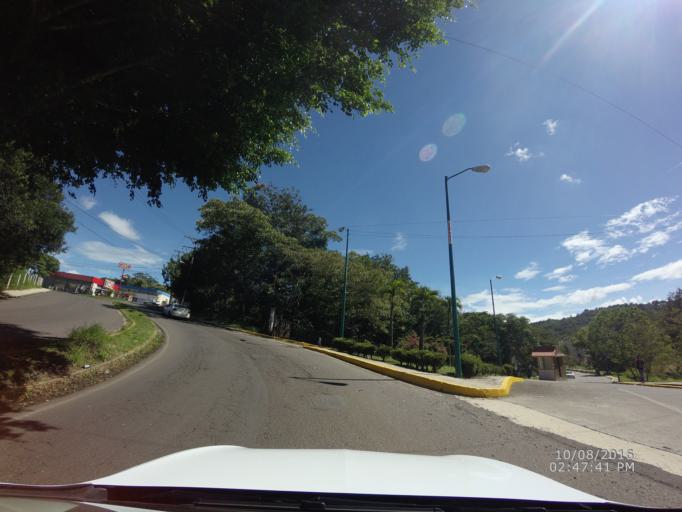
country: MX
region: Veracruz
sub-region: Xalapa
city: Lomas Verdes
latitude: 19.5048
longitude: -96.8913
